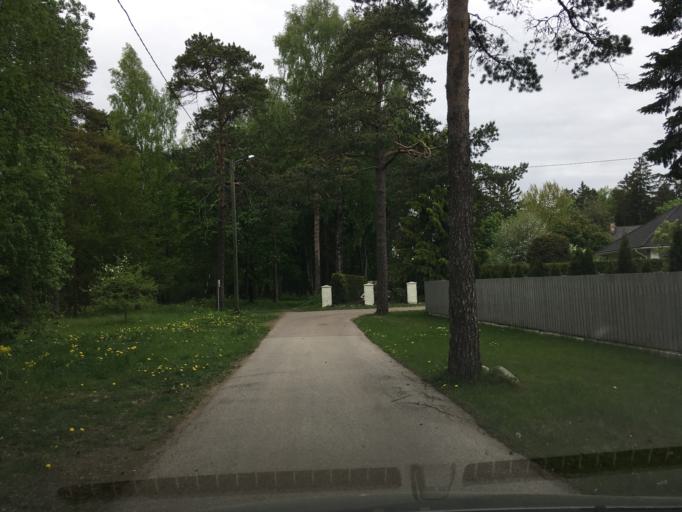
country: EE
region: Harju
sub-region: Saue vald
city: Laagri
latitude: 59.3865
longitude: 24.6545
